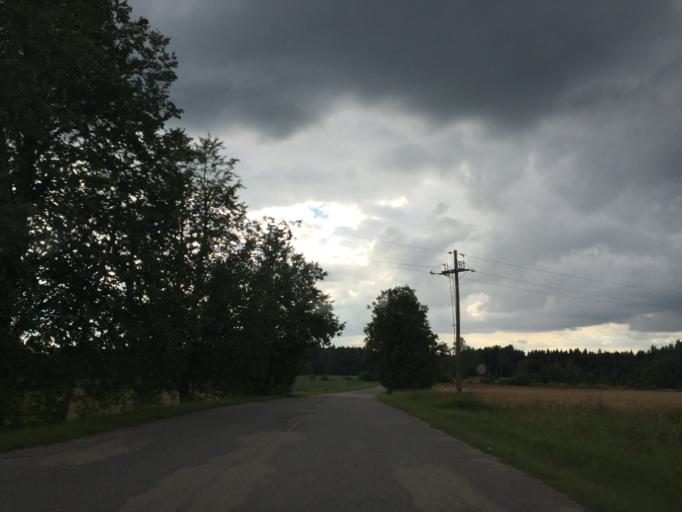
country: LV
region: Sigulda
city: Sigulda
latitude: 57.0813
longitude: 24.8354
